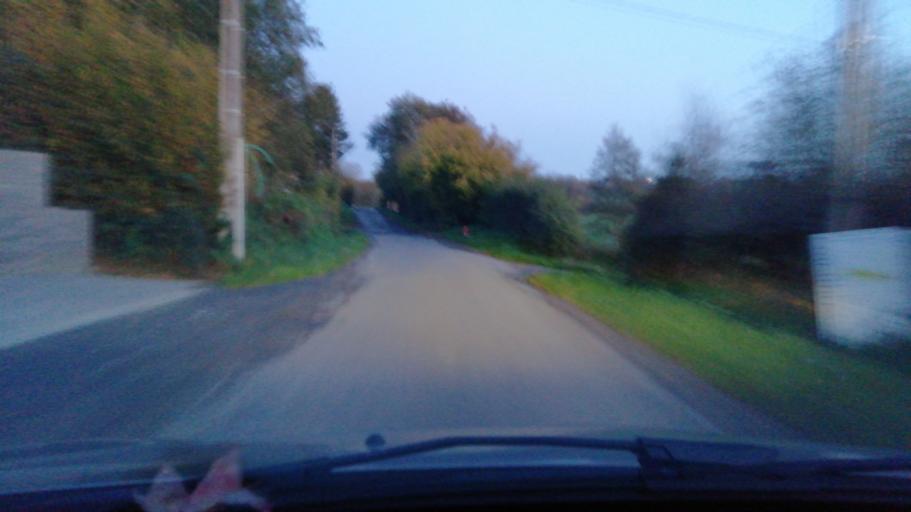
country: FR
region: Nord-Pas-de-Calais
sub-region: Departement du Nord
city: Marpent
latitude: 50.2562
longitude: 4.0888
